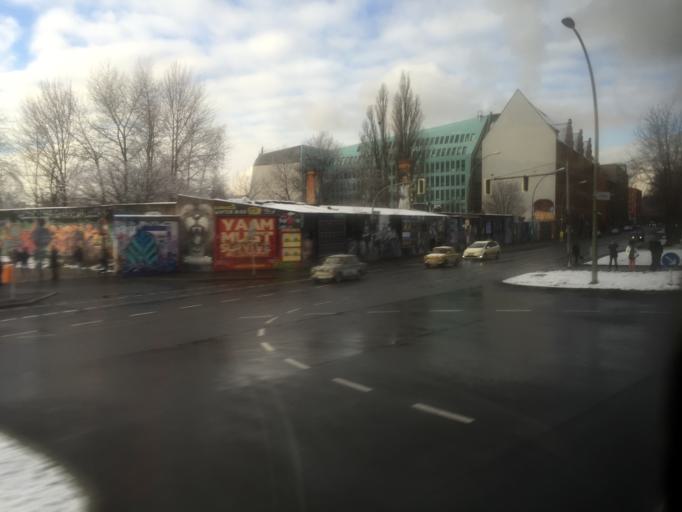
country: DE
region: Berlin
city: Berlin Treptow
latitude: 52.5084
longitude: 13.4350
